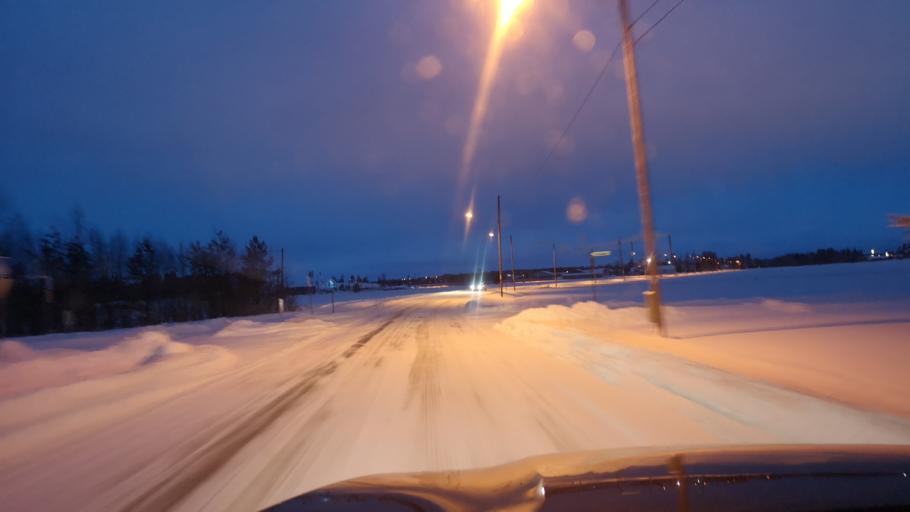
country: FI
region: Varsinais-Suomi
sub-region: Loimaa
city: Loimaa
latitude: 60.8633
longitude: 23.0812
